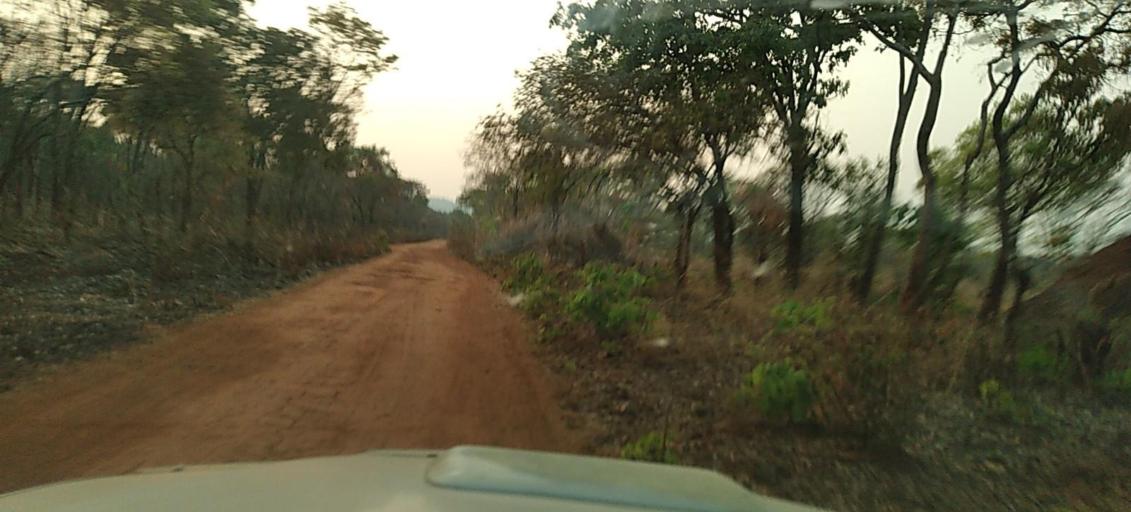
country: ZM
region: North-Western
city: Kasempa
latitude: -13.0760
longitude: 26.3884
